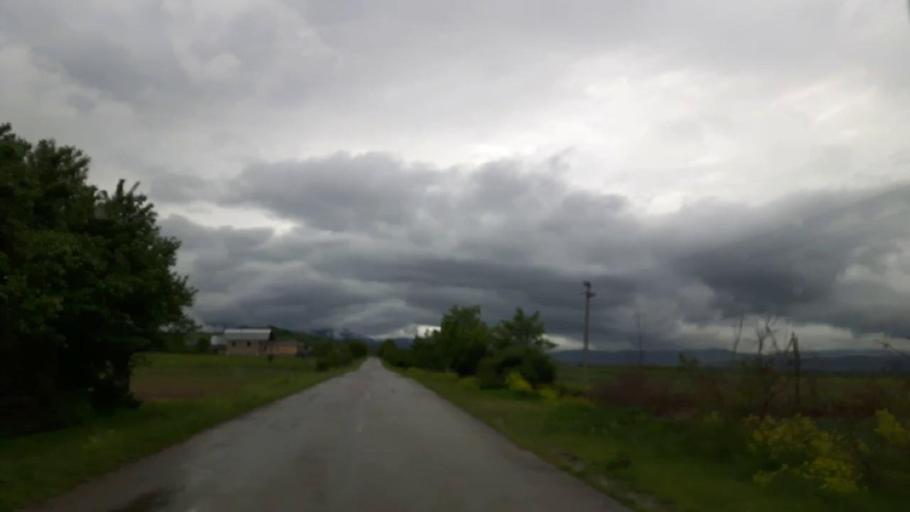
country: GE
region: Shida Kartli
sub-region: Khashuris Raioni
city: Khashuri
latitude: 41.9875
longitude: 43.6944
